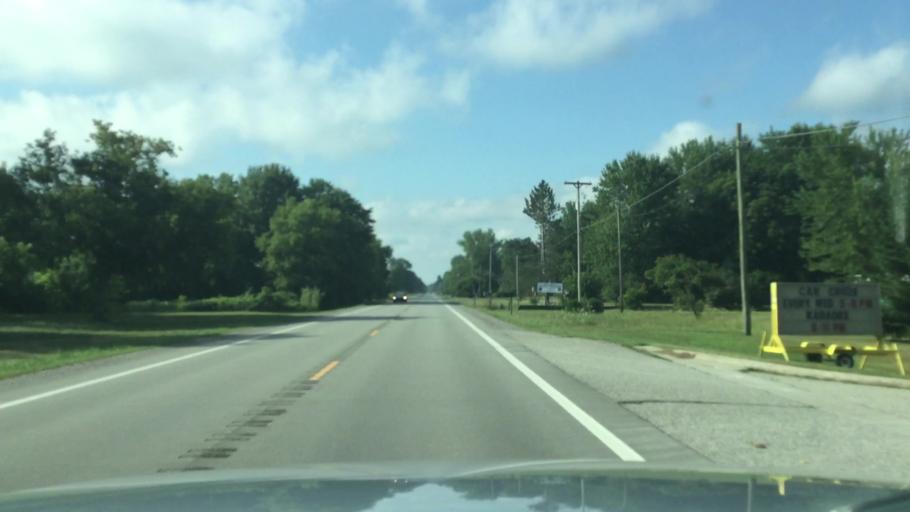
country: US
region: Michigan
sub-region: Saginaw County
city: Birch Run
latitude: 43.2453
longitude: -83.7354
